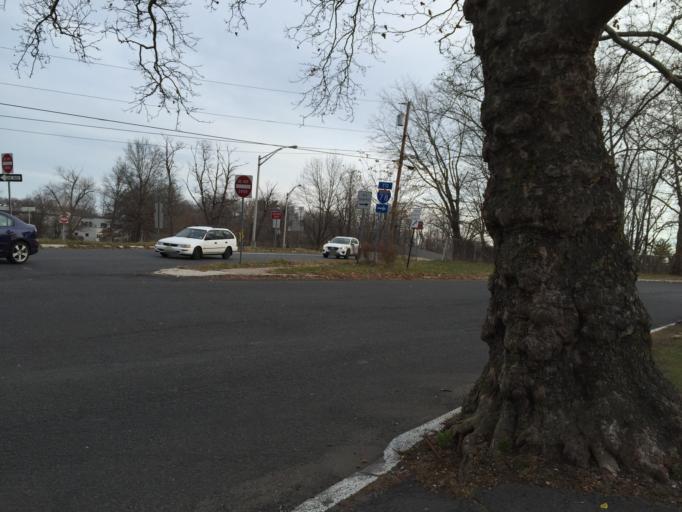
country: US
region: New Jersey
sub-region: Union County
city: Springfield
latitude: 40.7188
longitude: -74.3346
